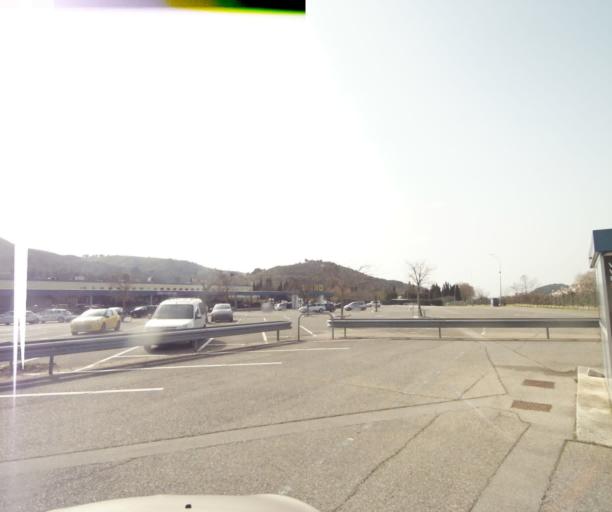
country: FR
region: Provence-Alpes-Cote d'Azur
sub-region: Departement des Bouches-du-Rhone
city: Les Pennes-Mirabeau
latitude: 43.4086
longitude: 5.3210
